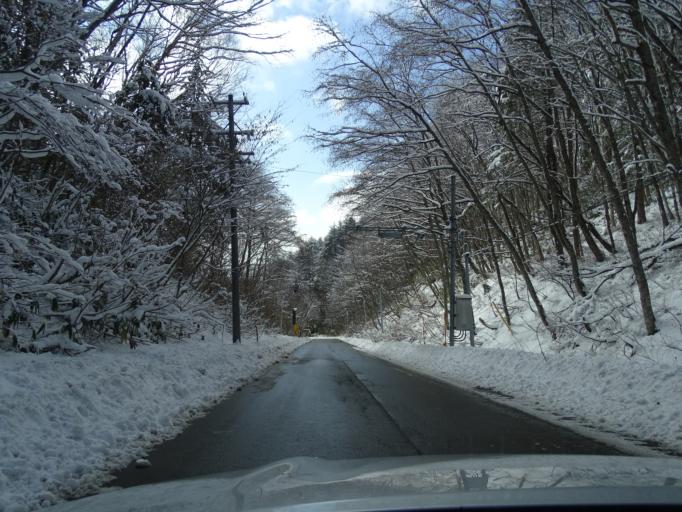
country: JP
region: Gifu
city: Takayama
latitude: 36.1431
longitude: 137.4223
